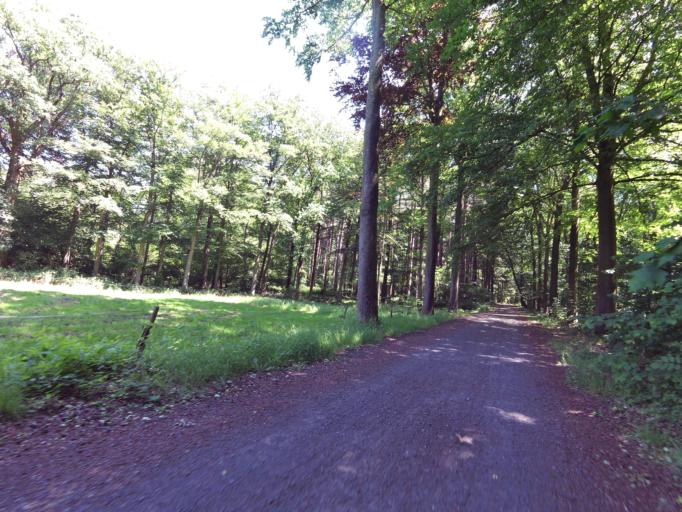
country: BE
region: Flanders
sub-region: Provincie West-Vlaanderen
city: Zedelgem
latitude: 51.1493
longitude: 3.1123
